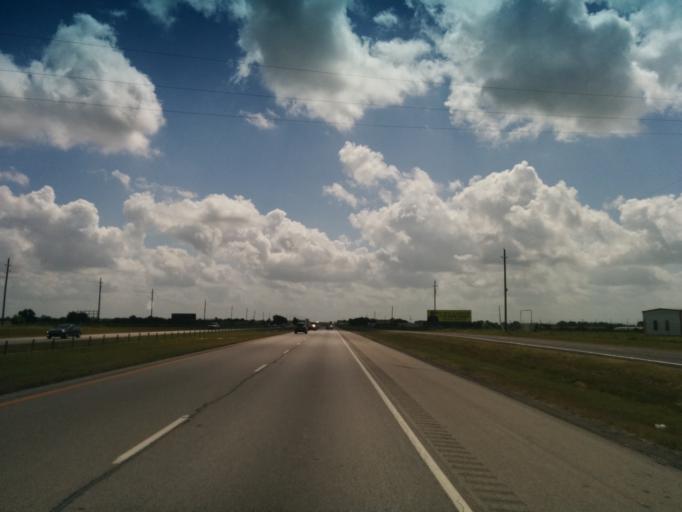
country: US
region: Texas
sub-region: Austin County
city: Sealy
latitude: 29.7551
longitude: -96.2471
